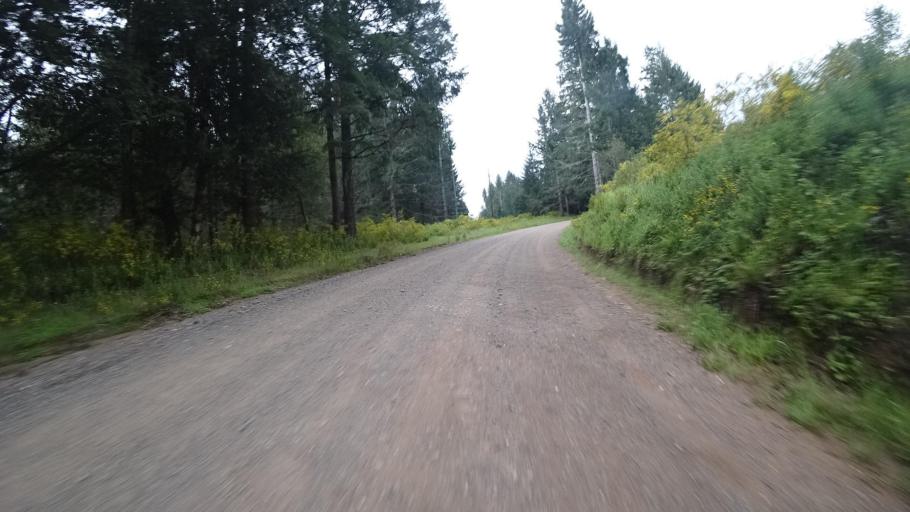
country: US
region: California
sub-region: Humboldt County
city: Redway
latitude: 40.2375
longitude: -123.7615
